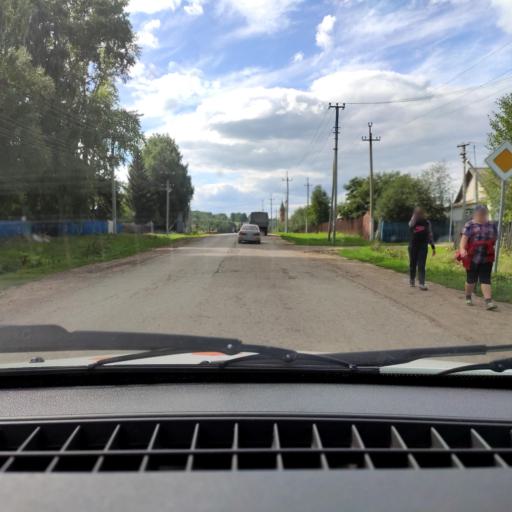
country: RU
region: Bashkortostan
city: Kudeyevskiy
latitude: 54.8821
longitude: 56.6364
